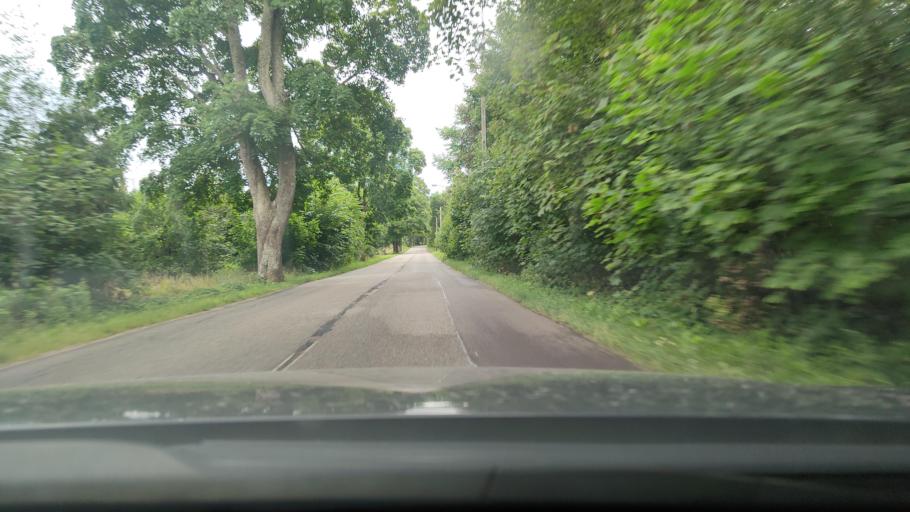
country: PL
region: Pomeranian Voivodeship
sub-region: Powiat pucki
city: Krokowa
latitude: 54.7571
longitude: 18.1707
